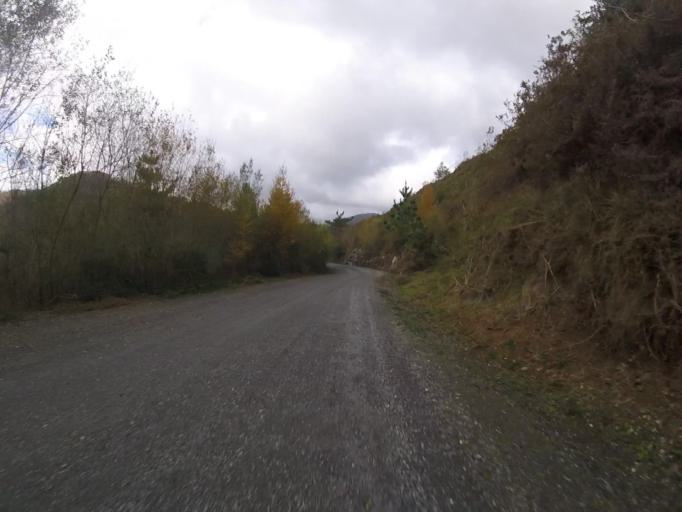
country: ES
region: Navarre
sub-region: Provincia de Navarra
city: Goizueta
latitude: 43.2181
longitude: -1.8297
